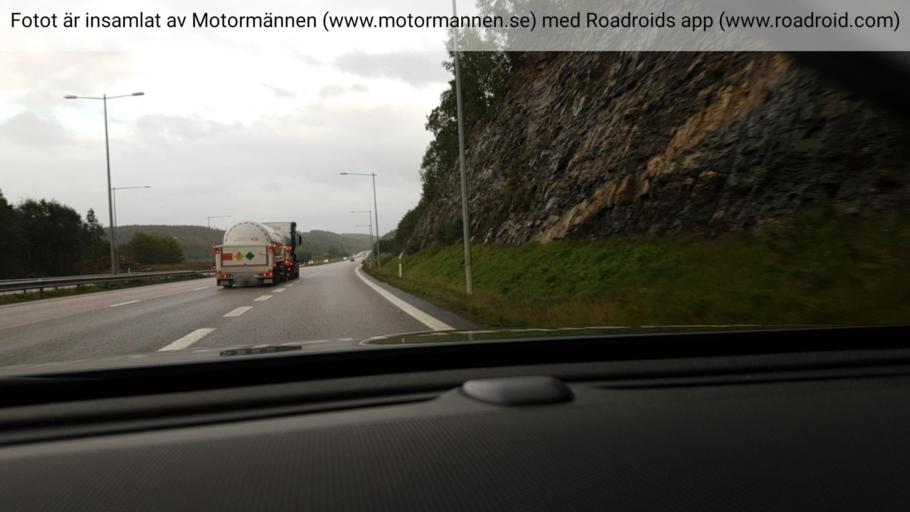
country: SE
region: Vaestra Goetaland
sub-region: Uddevalla Kommun
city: Ljungskile
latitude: 58.2885
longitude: 11.8747
